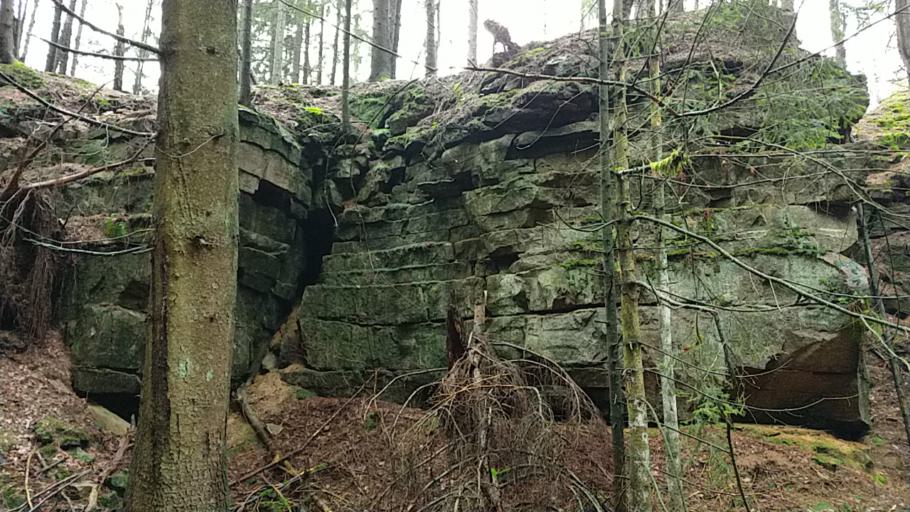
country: DE
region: Lower Saxony
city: Rehren
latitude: 52.2622
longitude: 9.1989
